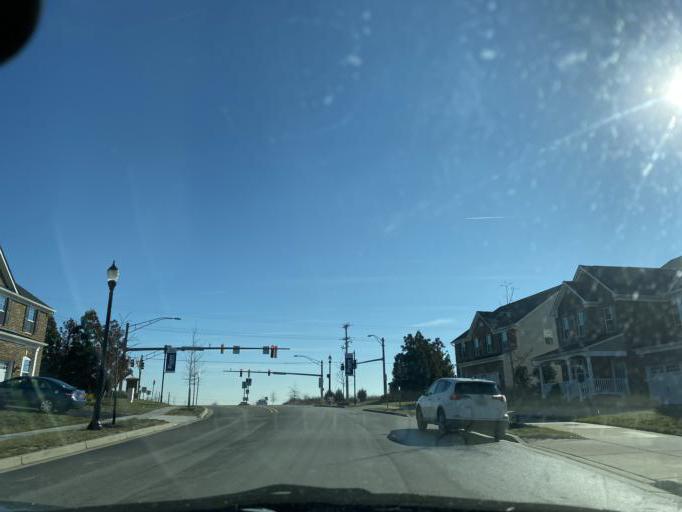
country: US
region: Maryland
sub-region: Prince George's County
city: West Laurel
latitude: 39.0900
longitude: -76.9159
